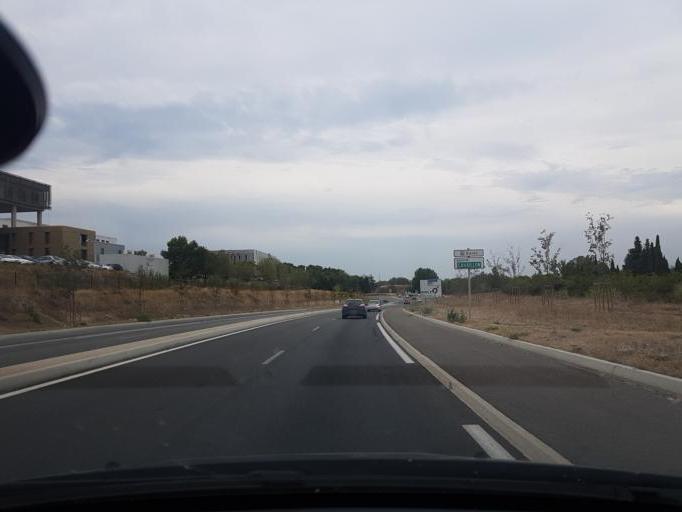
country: FR
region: Provence-Alpes-Cote d'Azur
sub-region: Departement du Vaucluse
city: Carpentras
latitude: 44.0487
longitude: 5.0276
